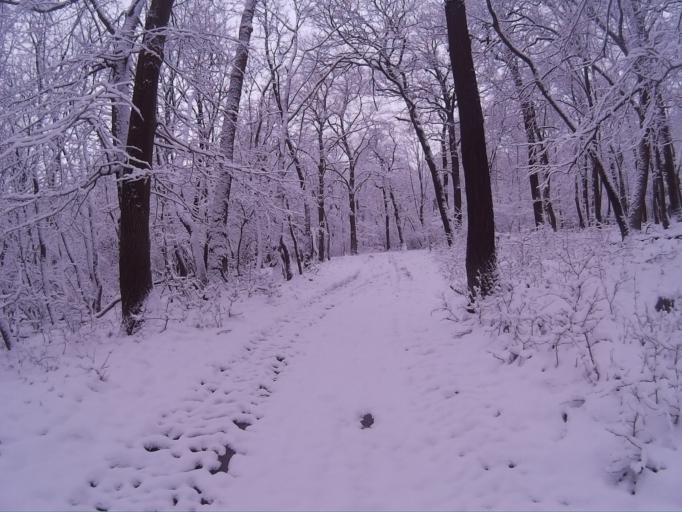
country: HU
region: Komarom-Esztergom
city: Tarjan
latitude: 47.5720
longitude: 18.5369
